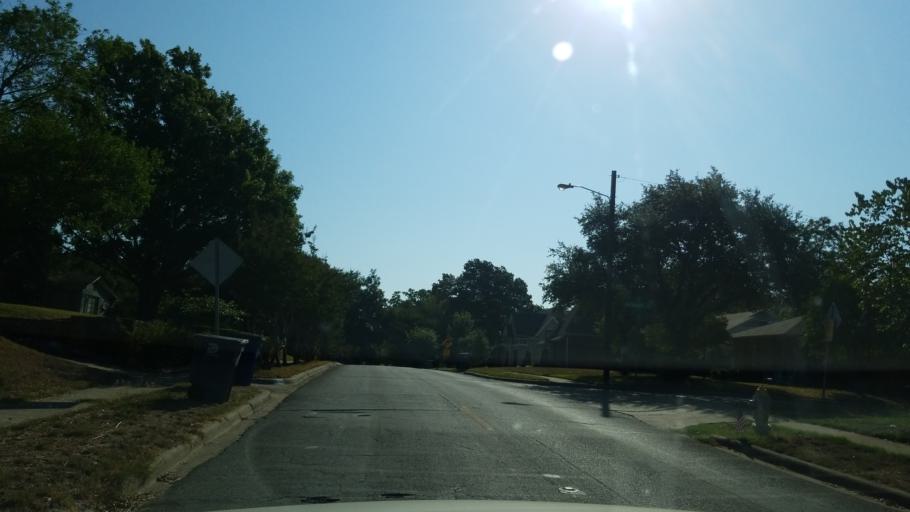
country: US
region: Texas
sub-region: Dallas County
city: Highland Park
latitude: 32.8107
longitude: -96.7375
